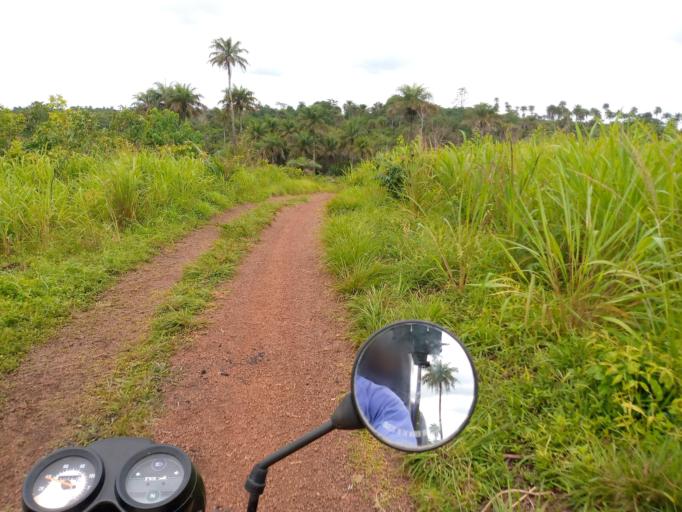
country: SL
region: Northern Province
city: Mange
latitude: 8.9907
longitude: -12.7705
